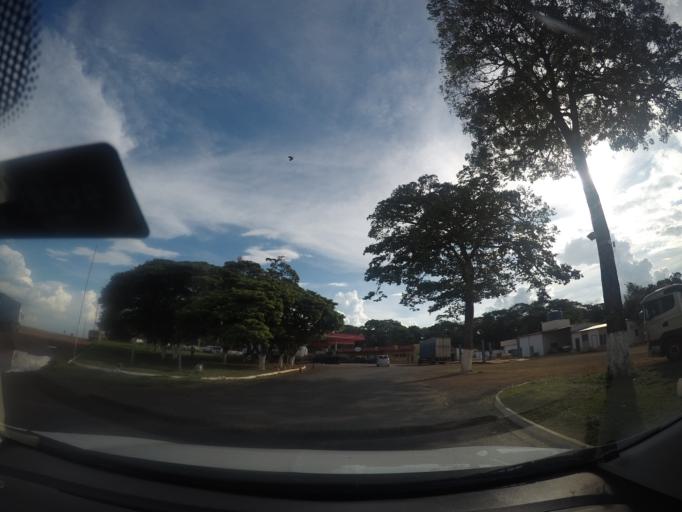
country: BR
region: Sao Paulo
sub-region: Jaboticabal
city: Jaboticabal
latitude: -21.3469
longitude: -48.3232
